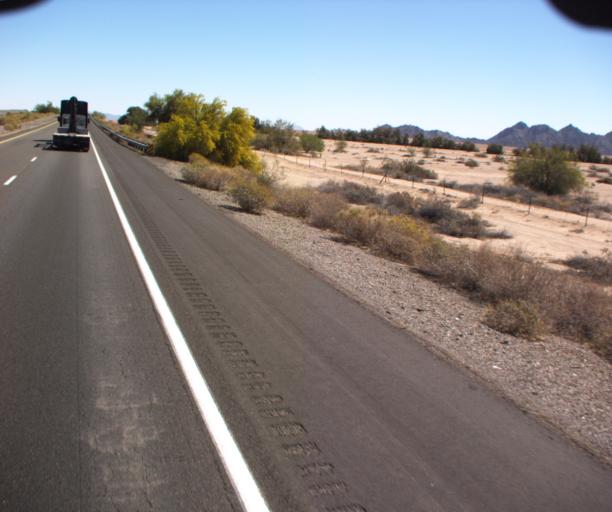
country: US
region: Arizona
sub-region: Yuma County
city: Wellton
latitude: 32.6758
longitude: -114.0547
